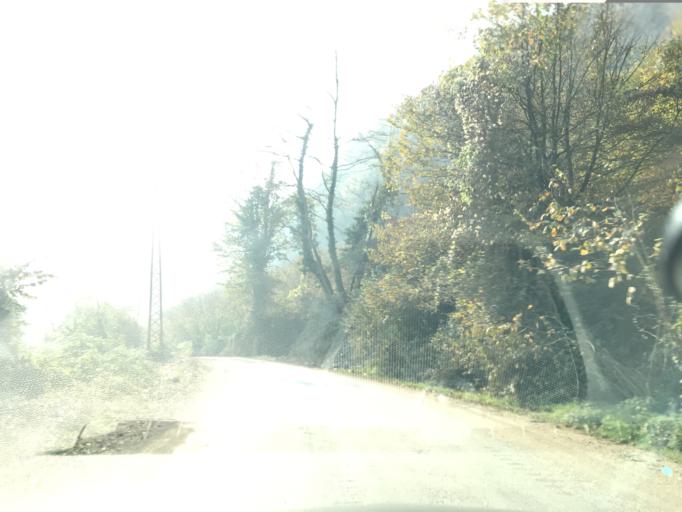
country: TR
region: Duzce
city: Cumayeri
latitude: 40.9221
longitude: 30.9287
